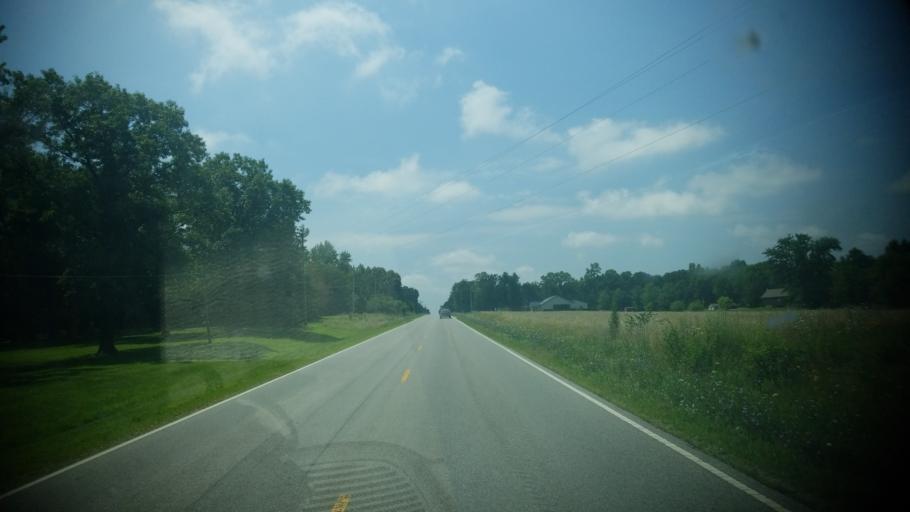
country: US
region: Illinois
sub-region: Wayne County
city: Fairfield
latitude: 38.4154
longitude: -88.3500
